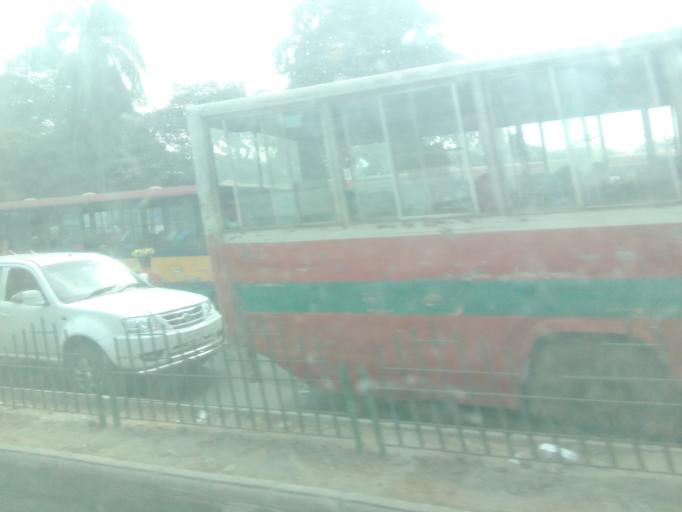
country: BD
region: Dhaka
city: Azimpur
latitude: 23.7377
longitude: 90.3982
